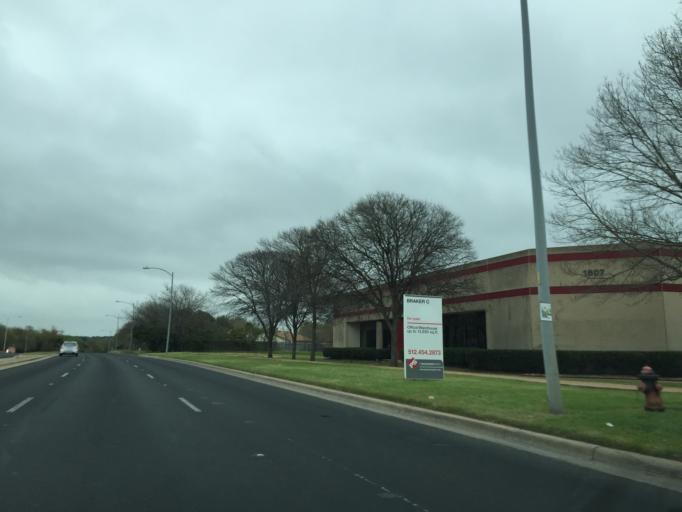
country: US
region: Texas
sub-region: Travis County
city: Wells Branch
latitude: 30.3911
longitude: -97.7056
